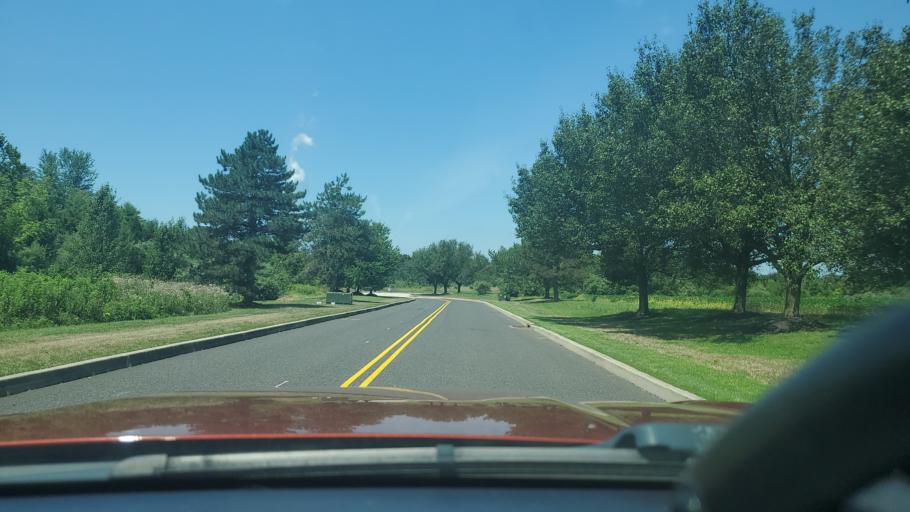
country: US
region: Pennsylvania
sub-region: Montgomery County
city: Limerick
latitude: 40.2245
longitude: -75.5528
